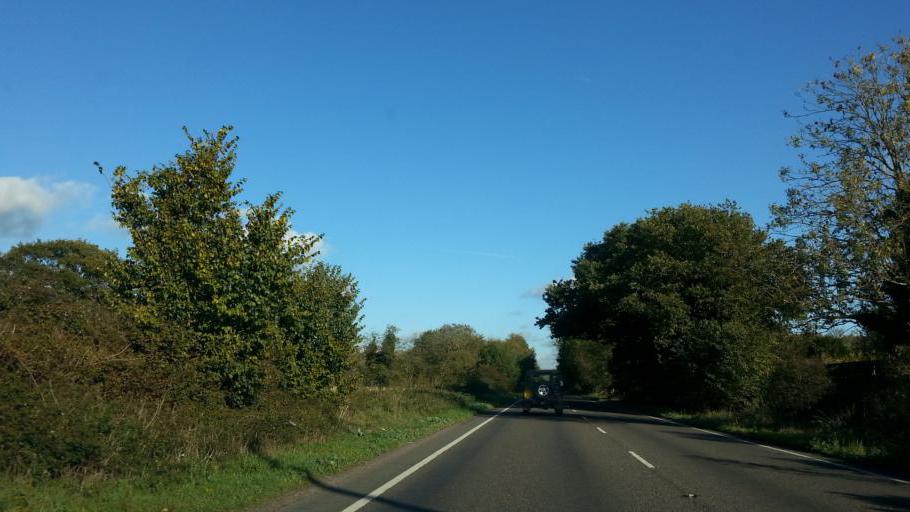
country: GB
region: England
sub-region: Suffolk
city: Bungay
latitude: 52.4539
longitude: 1.4199
